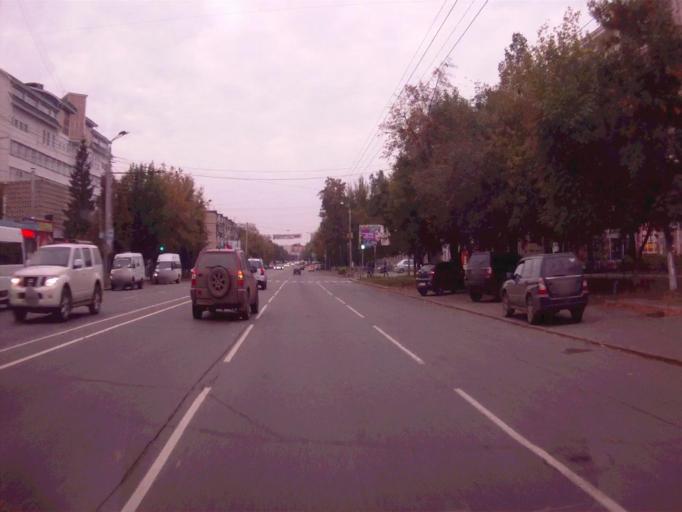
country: RU
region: Chelyabinsk
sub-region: Gorod Chelyabinsk
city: Chelyabinsk
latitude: 55.1538
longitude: 61.4143
